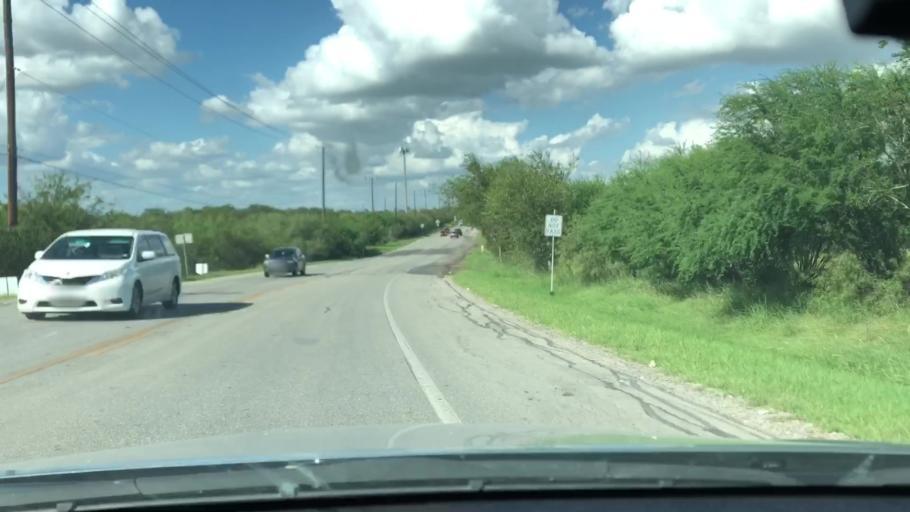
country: US
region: Texas
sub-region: Bexar County
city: Converse
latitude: 29.4777
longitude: -98.3137
